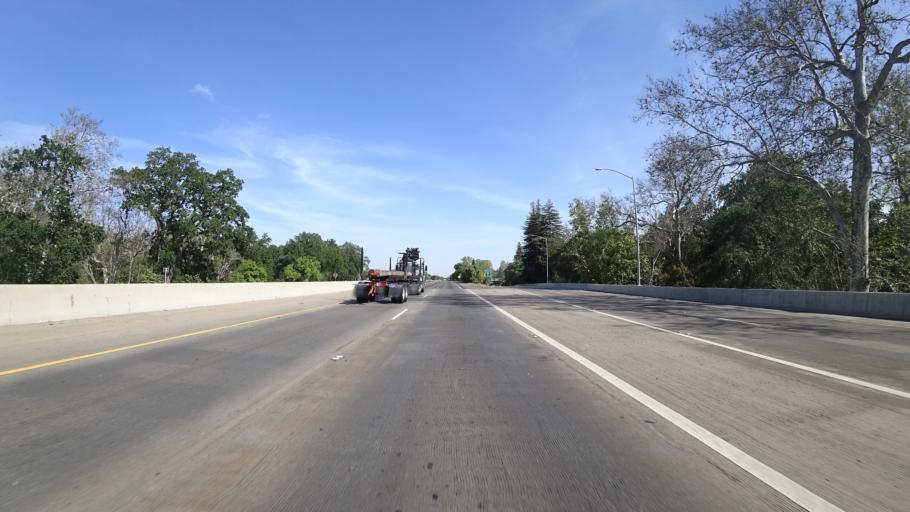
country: US
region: California
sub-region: Butte County
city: Chico
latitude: 39.7387
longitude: -121.8228
